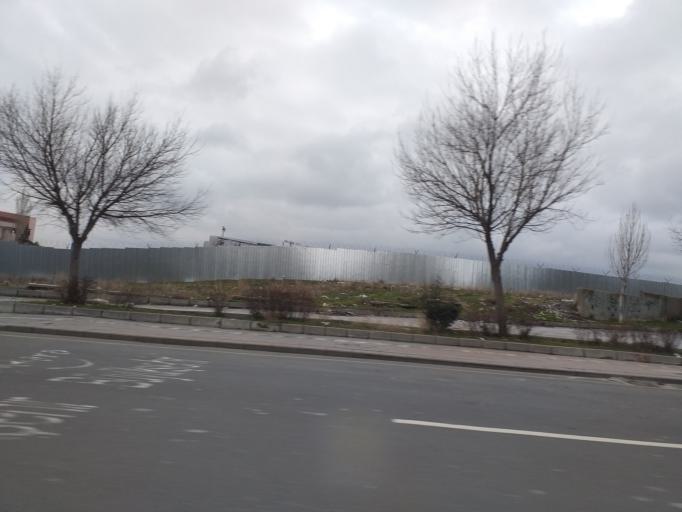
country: TR
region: Ankara
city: Ankara
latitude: 39.9688
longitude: 32.8364
